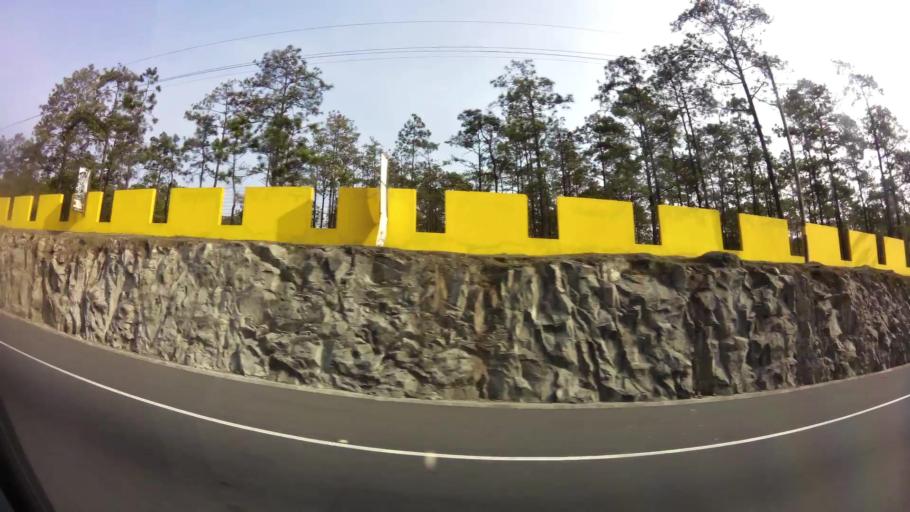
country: HN
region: Francisco Morazan
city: Zambrano
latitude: 14.2903
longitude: -87.4170
